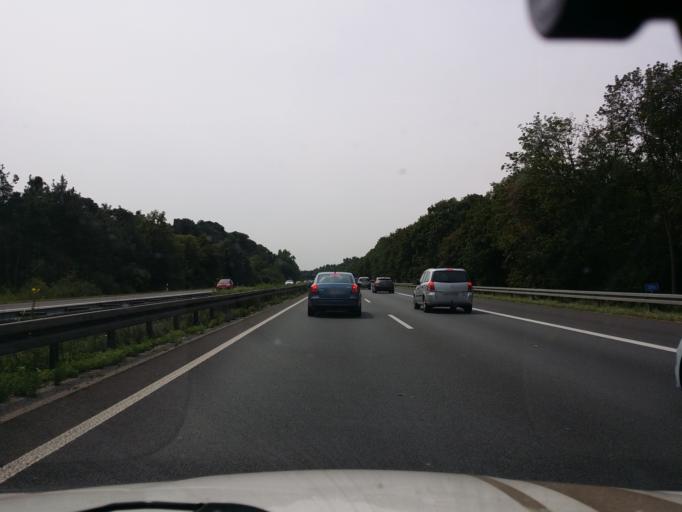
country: DE
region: Hesse
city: Pfungstadt
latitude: 49.8019
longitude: 8.6247
